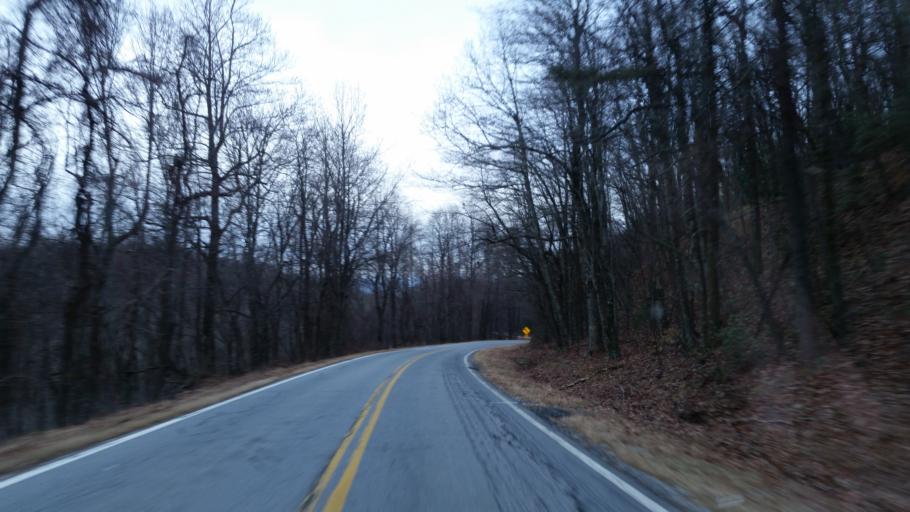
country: US
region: Georgia
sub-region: Pickens County
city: Jasper
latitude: 34.5457
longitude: -84.3273
